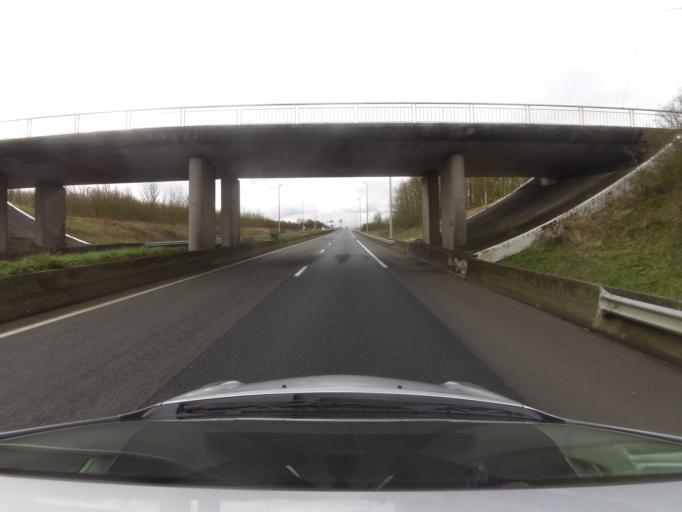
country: FR
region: Nord-Pas-de-Calais
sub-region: Departement du Pas-de-Calais
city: Marquise
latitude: 50.8074
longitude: 1.6935
